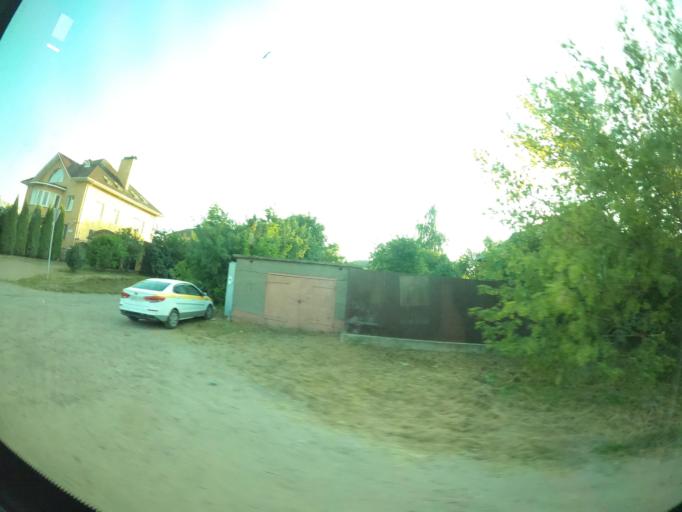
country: RU
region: Moskovskaya
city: Serpukhov
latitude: 54.9321
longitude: 37.3671
